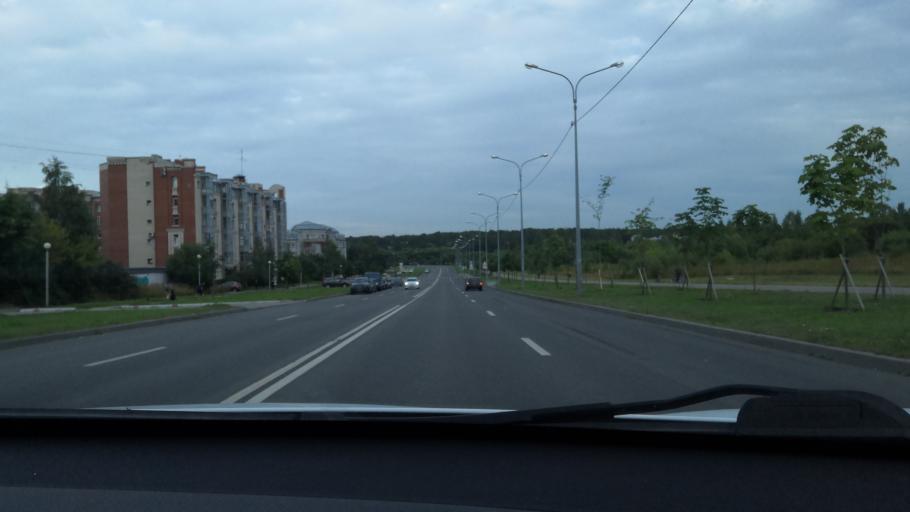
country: RU
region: St.-Petersburg
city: Pavlovsk
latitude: 59.6943
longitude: 30.4212
